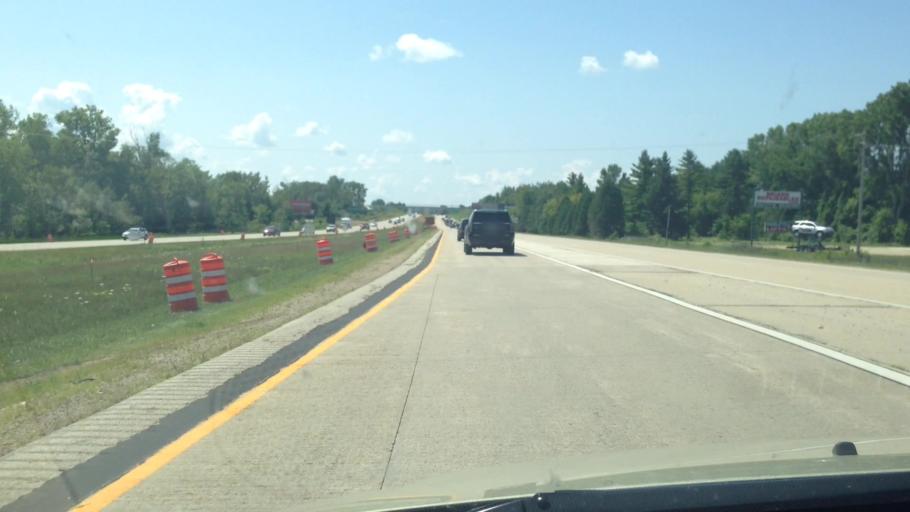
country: US
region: Wisconsin
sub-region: Oconto County
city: Oconto Falls
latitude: 44.7858
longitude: -88.0466
